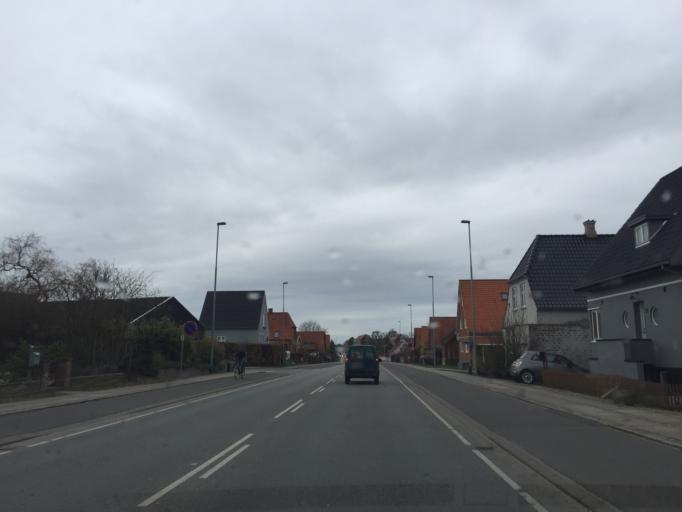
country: DK
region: South Denmark
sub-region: Odense Kommune
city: Odense
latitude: 55.3948
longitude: 10.3392
